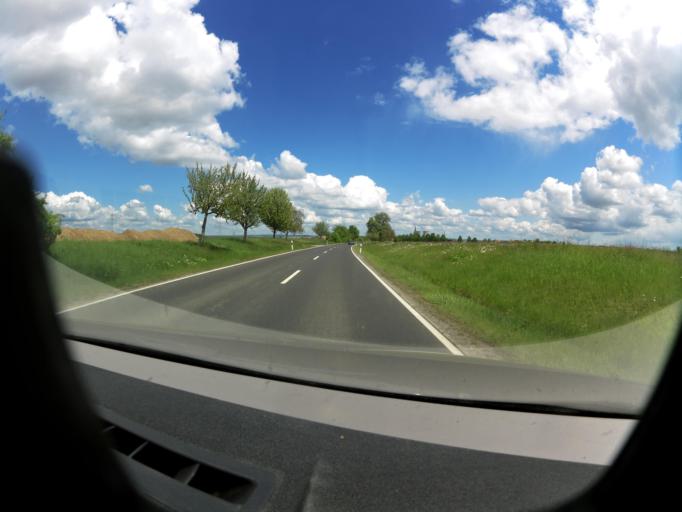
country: DE
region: Bavaria
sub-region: Regierungsbezirk Unterfranken
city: Waigolshausen
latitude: 49.9574
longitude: 10.1475
